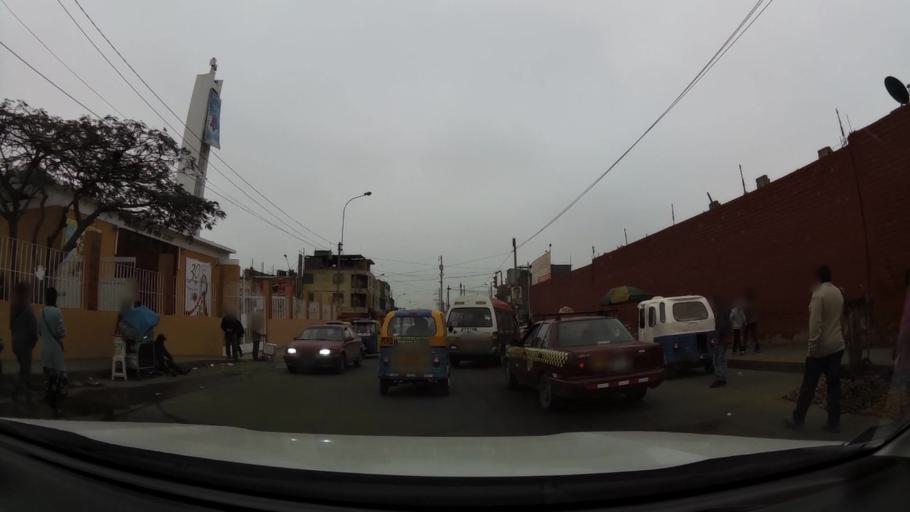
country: PE
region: Lima
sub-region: Lima
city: Surco
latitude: -12.1500
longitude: -76.9701
